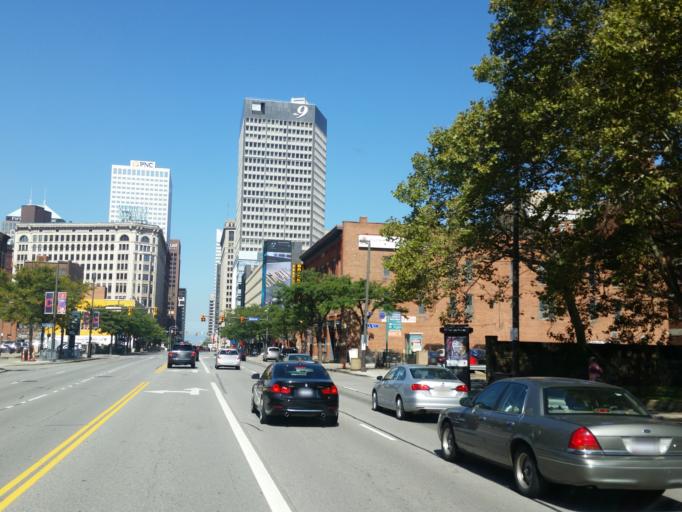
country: US
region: Ohio
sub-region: Cuyahoga County
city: Cleveland
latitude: 41.4971
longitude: -81.6839
